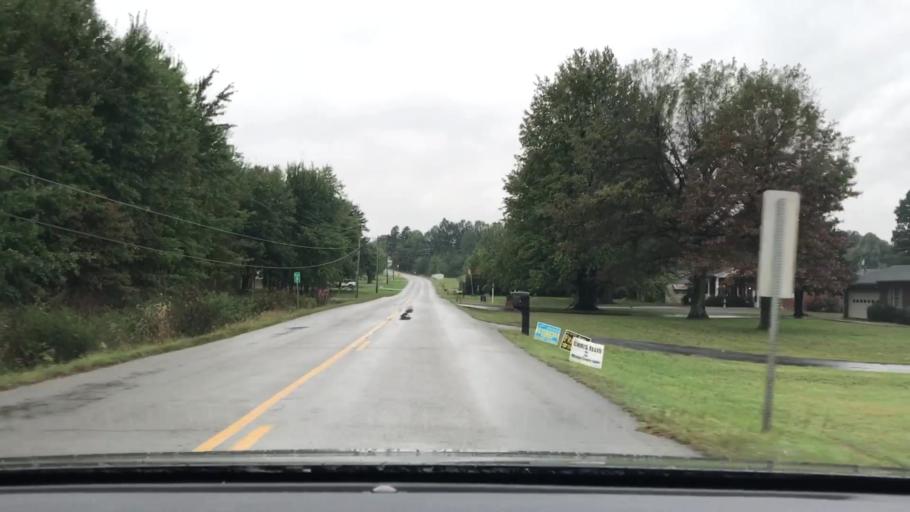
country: US
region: Kentucky
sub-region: McLean County
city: Calhoun
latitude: 37.4245
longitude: -87.2606
